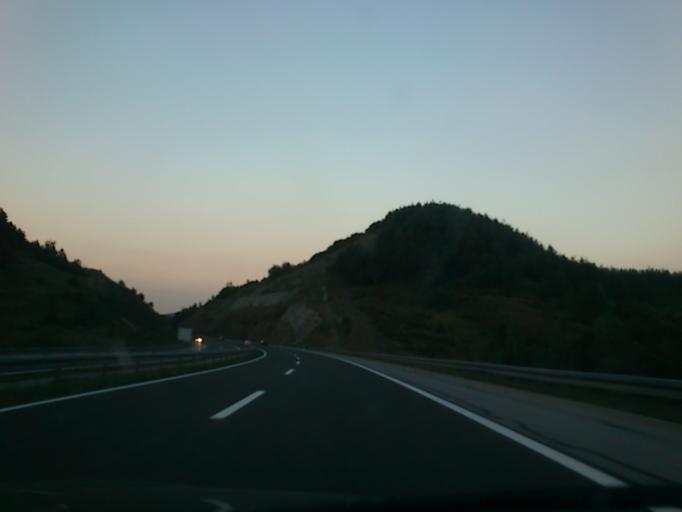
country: HR
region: Karlovacka
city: Ostarije
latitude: 45.1422
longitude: 15.2713
